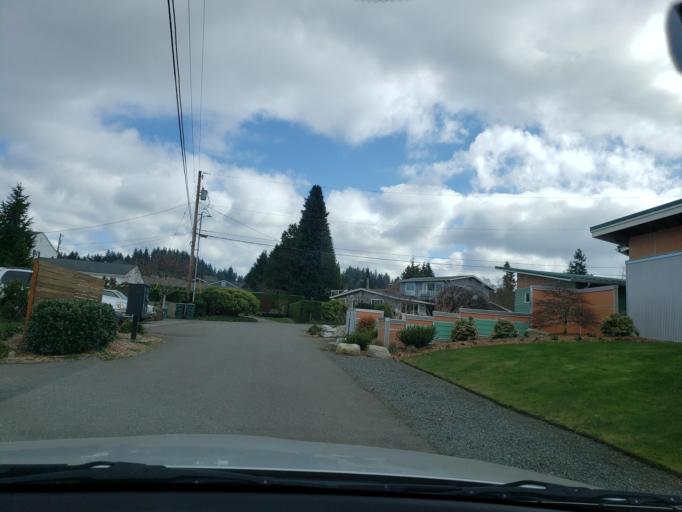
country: US
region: Washington
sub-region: Snohomish County
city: Edmonds
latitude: 47.8206
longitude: -122.3705
